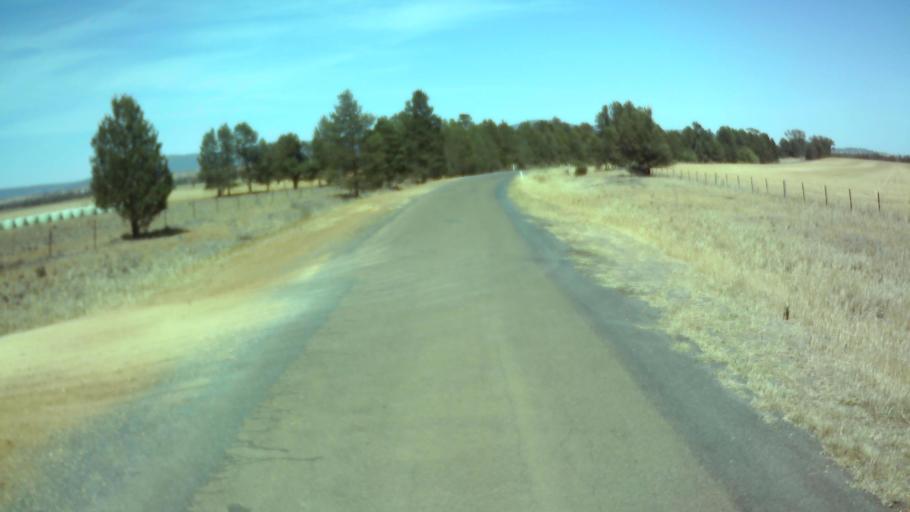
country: AU
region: New South Wales
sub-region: Weddin
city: Grenfell
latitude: -33.8709
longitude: 148.1041
